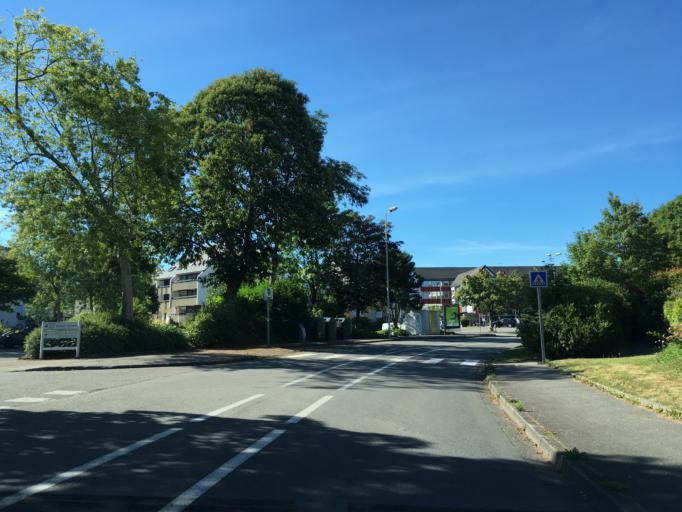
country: FR
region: Brittany
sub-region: Departement du Finistere
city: Quimper
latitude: 47.9849
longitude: -4.0832
